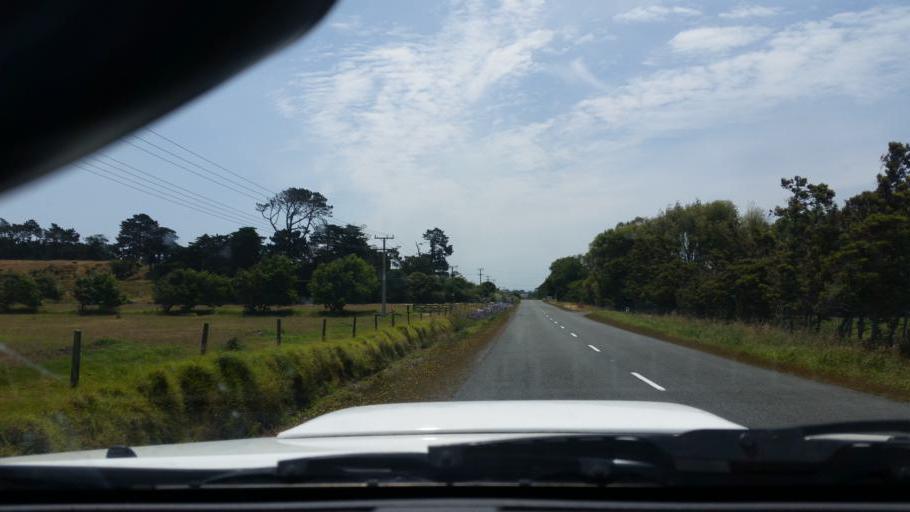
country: NZ
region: Northland
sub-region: Kaipara District
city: Dargaville
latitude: -36.0618
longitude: 173.9368
